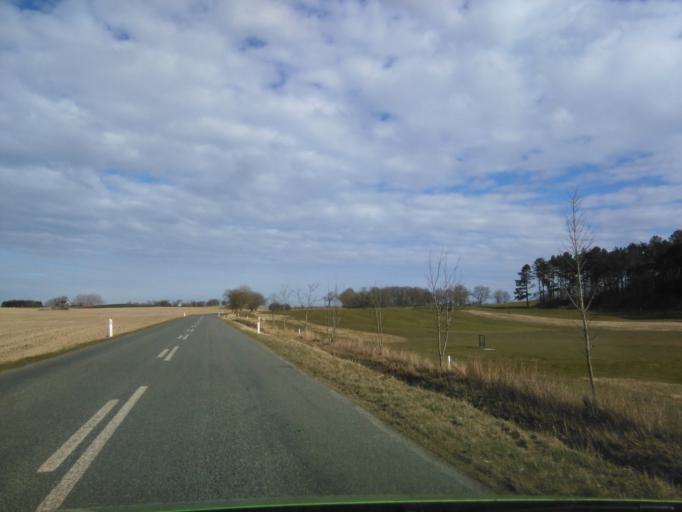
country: DK
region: Central Jutland
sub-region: Odder Kommune
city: Odder
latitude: 55.9489
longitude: 10.0999
